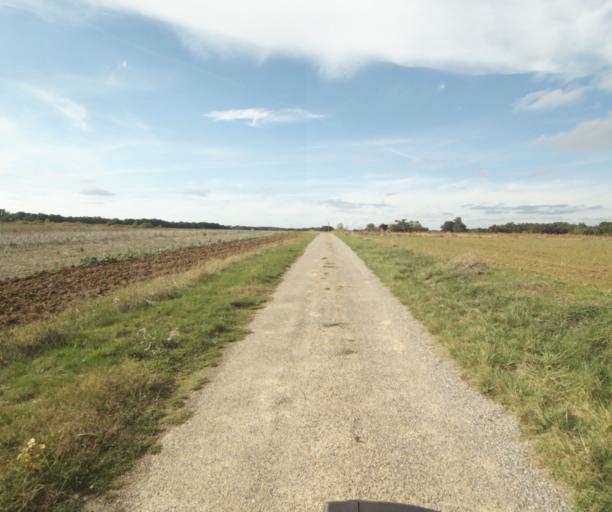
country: FR
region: Midi-Pyrenees
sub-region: Departement du Tarn-et-Garonne
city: Saint-Porquier
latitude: 43.9500
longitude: 1.1419
